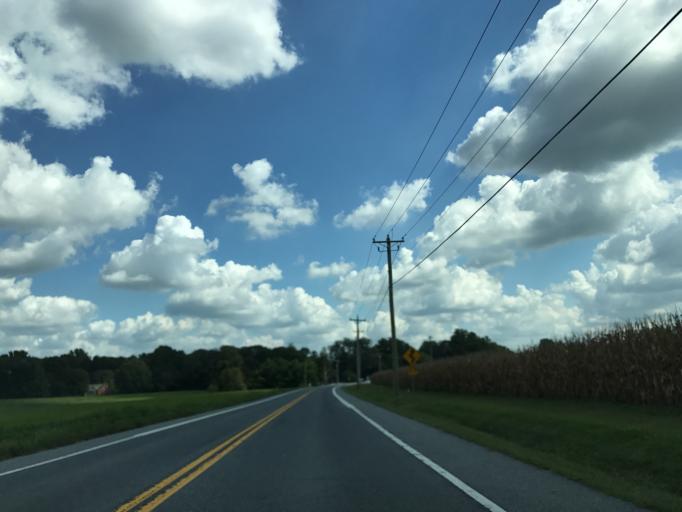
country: US
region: Maryland
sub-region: Caroline County
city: Ridgely
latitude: 39.0095
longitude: -75.9438
